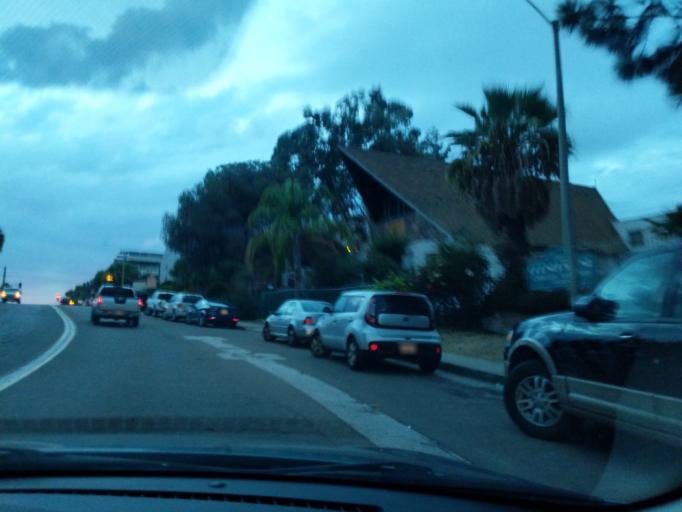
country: US
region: California
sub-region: San Diego County
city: San Diego
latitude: 32.7159
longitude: -117.1280
